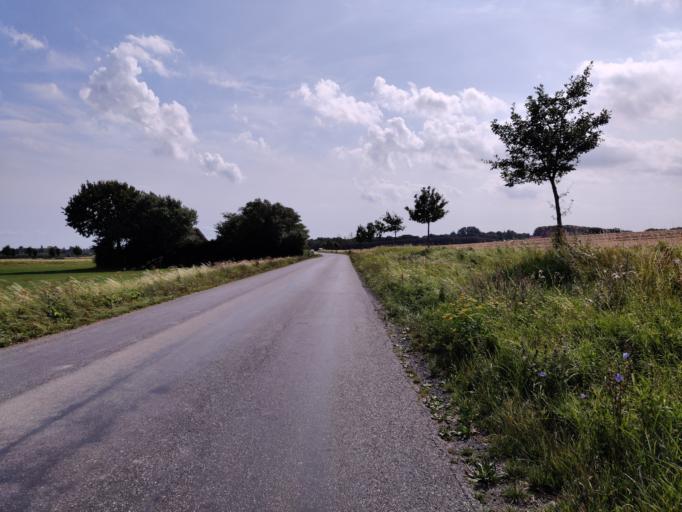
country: DK
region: Zealand
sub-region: Guldborgsund Kommune
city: Nykobing Falster
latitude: 54.6549
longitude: 11.8876
